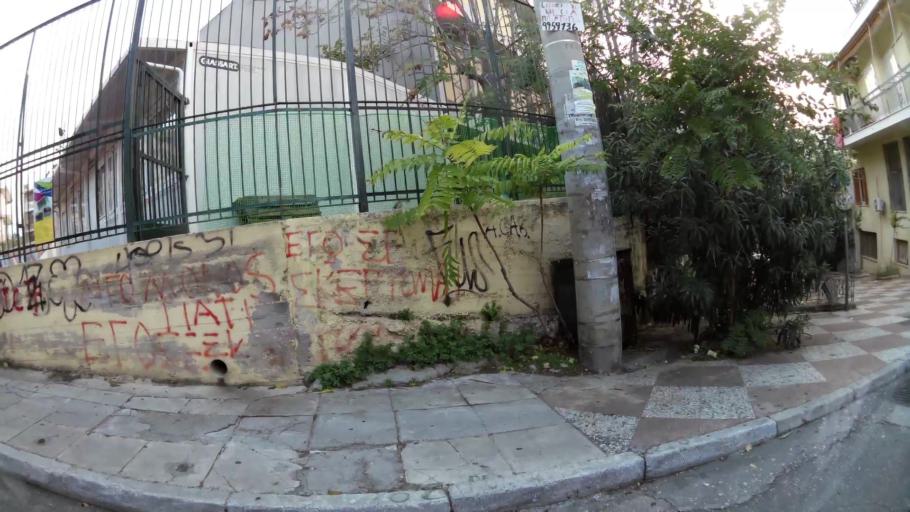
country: GR
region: Attica
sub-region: Nomarchia Athinas
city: Dhafni
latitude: 37.9540
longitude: 23.7284
